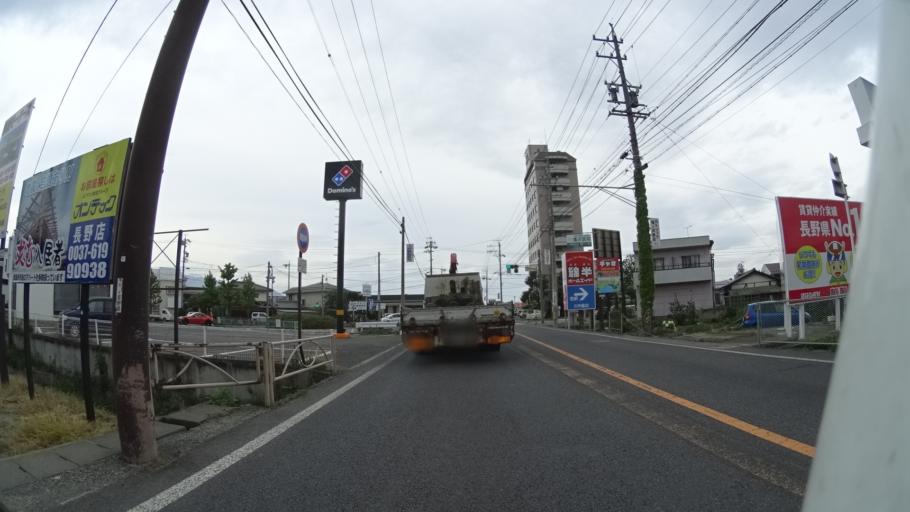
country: JP
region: Nagano
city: Nagano-shi
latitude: 36.5812
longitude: 138.1483
